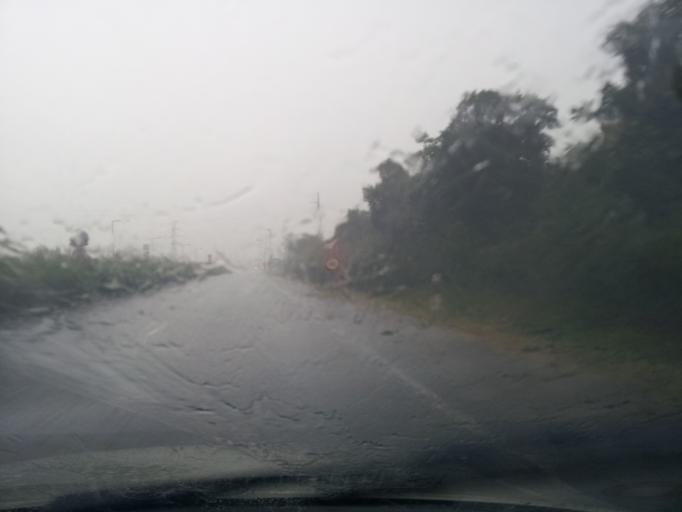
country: HU
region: Borsod-Abauj-Zemplen
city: Felsozsolca
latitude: 48.1141
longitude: 20.8634
